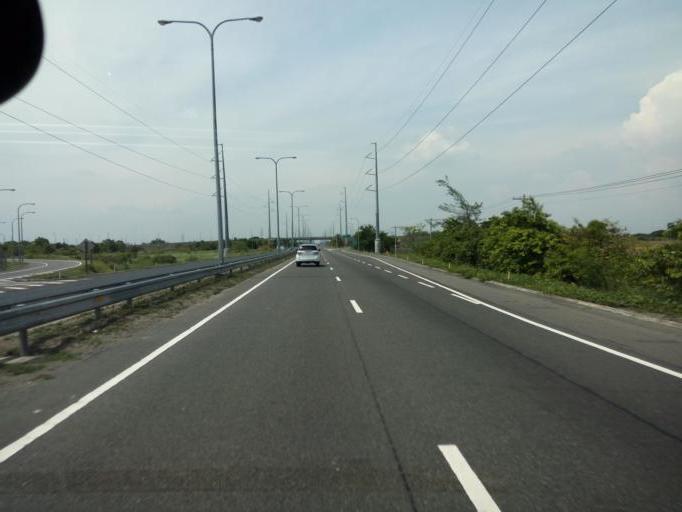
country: PH
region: Central Luzon
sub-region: Province of Tarlac
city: Santo Nino
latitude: 15.3149
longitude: 120.6224
